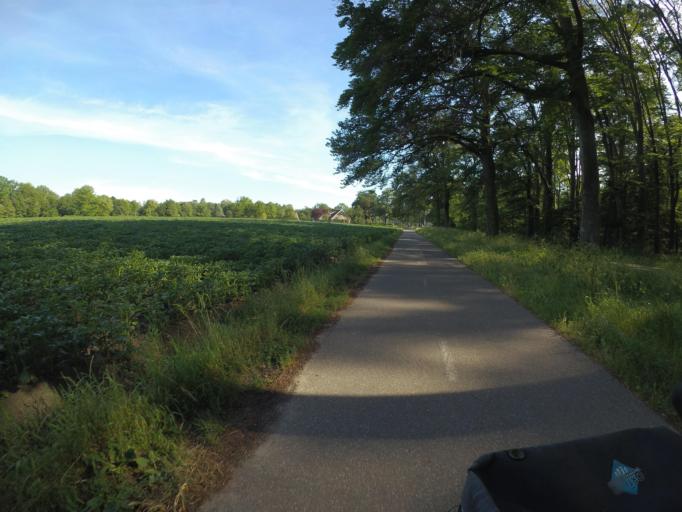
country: NL
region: Gelderland
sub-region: Gemeente Winterswijk
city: Winterswijk
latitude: 51.9886
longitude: 6.7273
